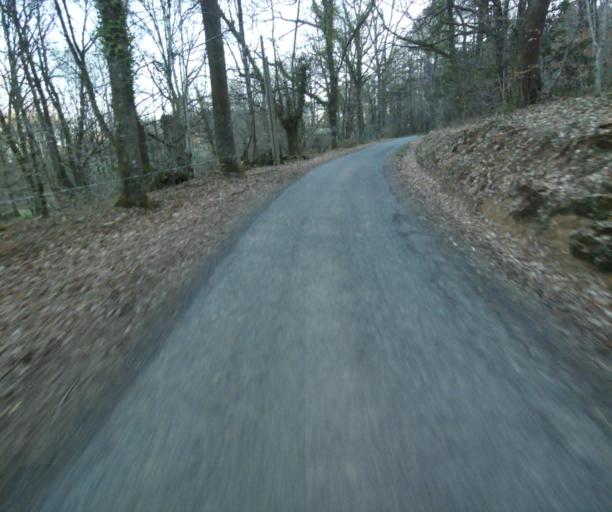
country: FR
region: Limousin
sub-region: Departement de la Correze
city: Seilhac
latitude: 45.3493
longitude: 1.7207
